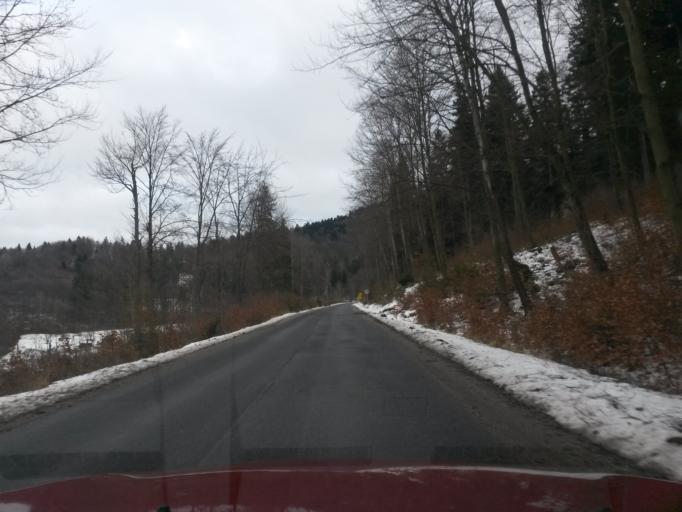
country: SK
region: Presovsky
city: Spisske Podhradie
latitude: 48.8778
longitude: 20.6998
